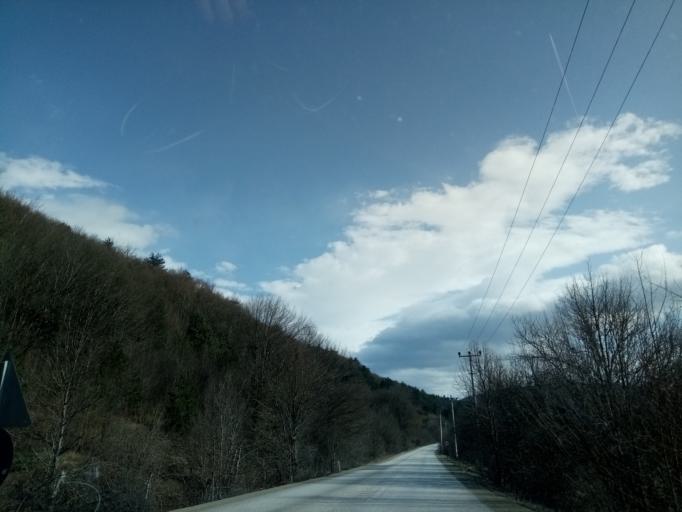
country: TR
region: Duzce
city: Kaynasli
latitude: 40.6581
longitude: 31.3977
